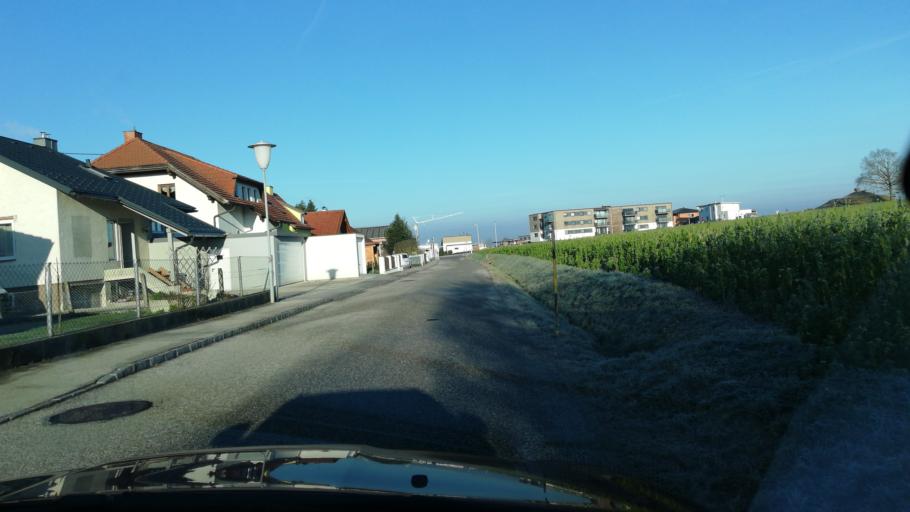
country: AT
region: Upper Austria
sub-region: Politischer Bezirk Steyr-Land
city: Bad Hall
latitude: 48.0352
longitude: 14.2154
